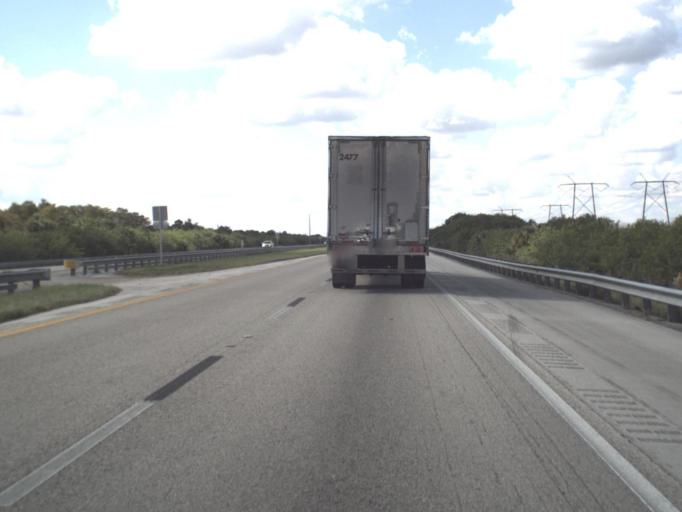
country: US
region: Florida
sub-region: Indian River County
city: West Vero Corridor
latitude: 27.5595
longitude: -80.6603
